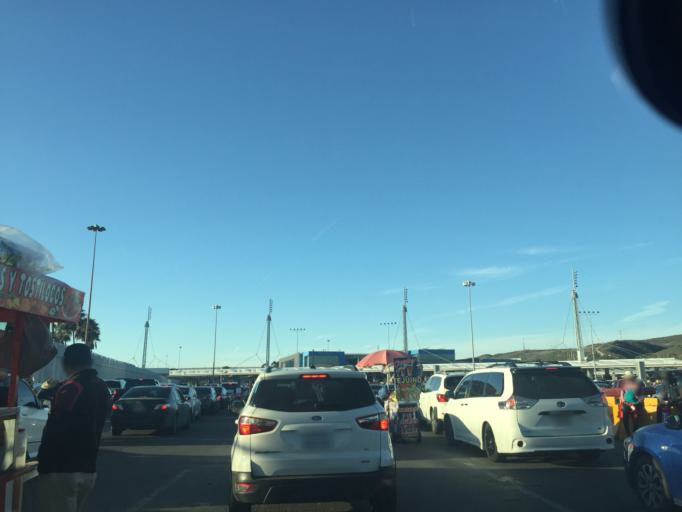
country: MX
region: Baja California
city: Tijuana
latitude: 32.5413
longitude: -117.0284
